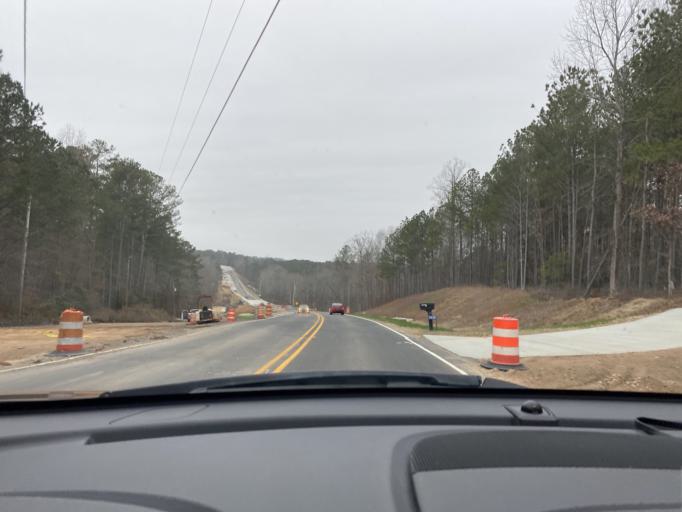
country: US
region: Georgia
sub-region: Gwinnett County
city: Dacula
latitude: 33.9169
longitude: -83.8845
